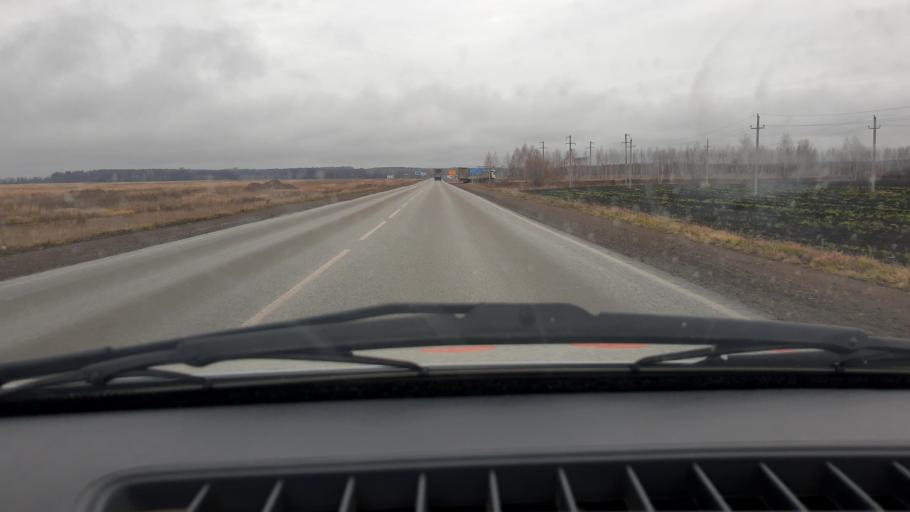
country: RU
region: Bashkortostan
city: Iglino
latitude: 54.7539
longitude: 56.2846
